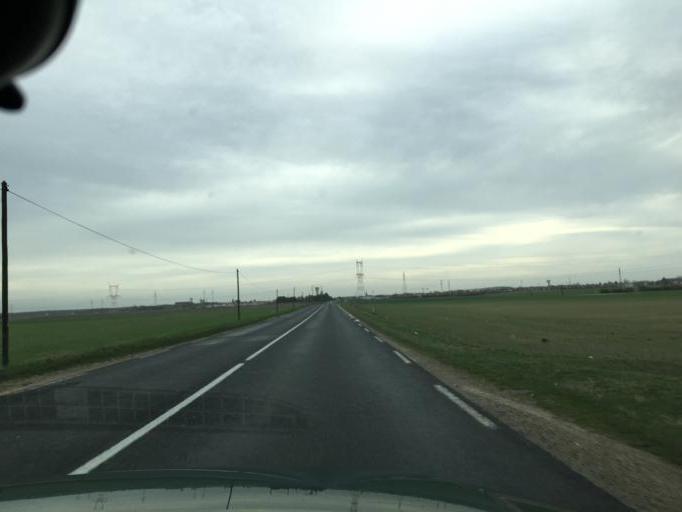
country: FR
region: Centre
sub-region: Departement du Loiret
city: Ormes
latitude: 47.9395
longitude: 1.7934
